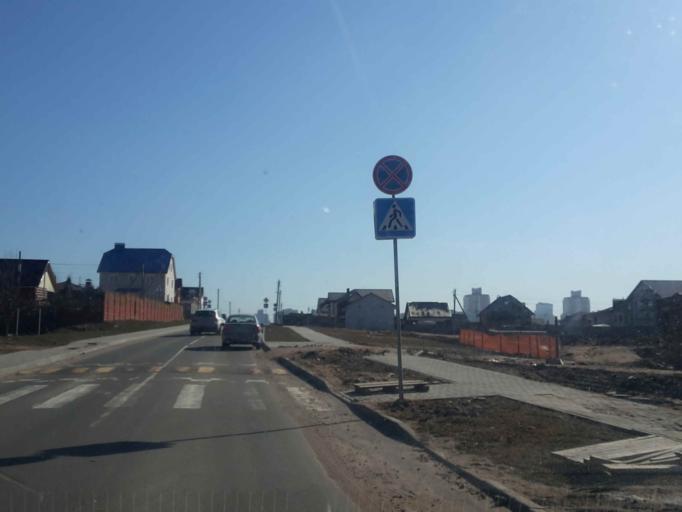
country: BY
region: Minsk
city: Zhdanovichy
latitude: 53.9204
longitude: 27.4056
